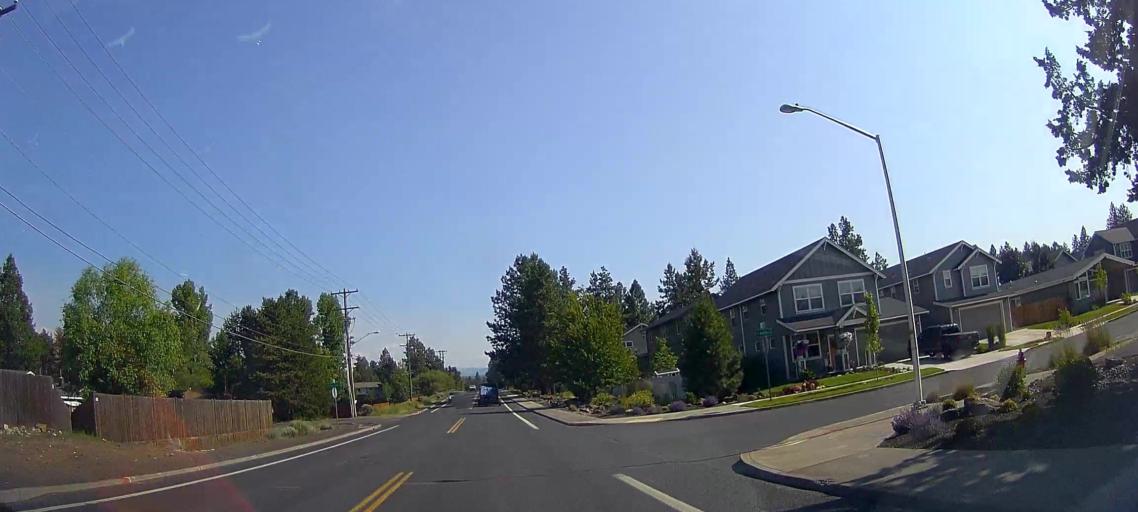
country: US
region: Oregon
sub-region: Deschutes County
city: Bend
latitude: 44.0344
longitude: -121.2838
